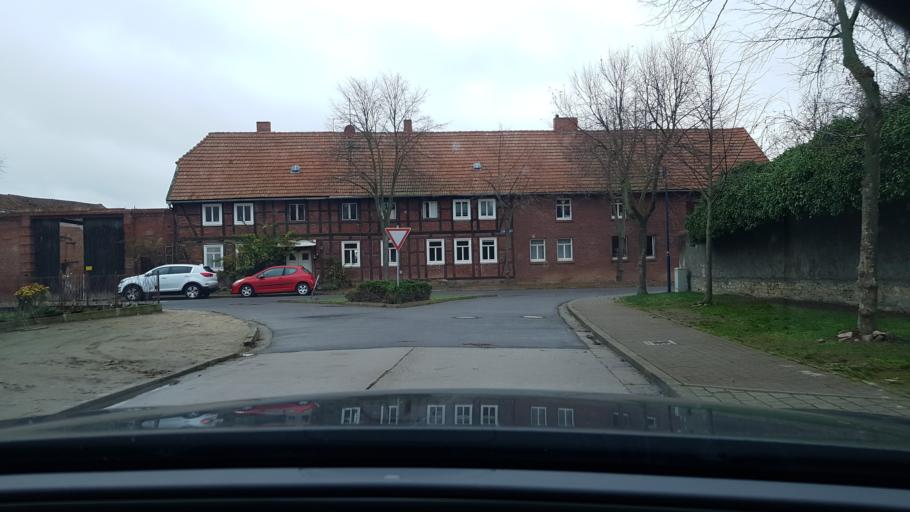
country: DE
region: Saxony-Anhalt
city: Weferlingen
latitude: 52.4018
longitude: 11.1130
